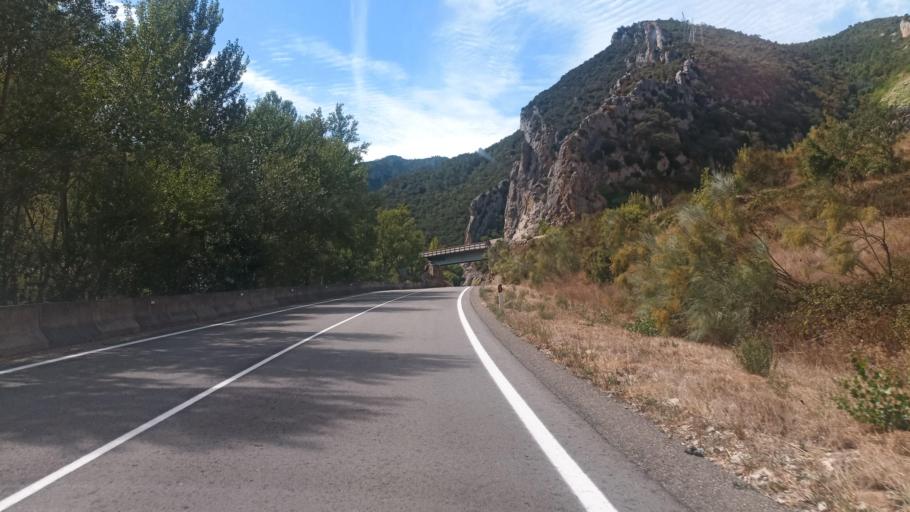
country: ES
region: Castille and Leon
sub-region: Provincia de Burgos
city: Trespaderne
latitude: 42.7932
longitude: -3.4029
